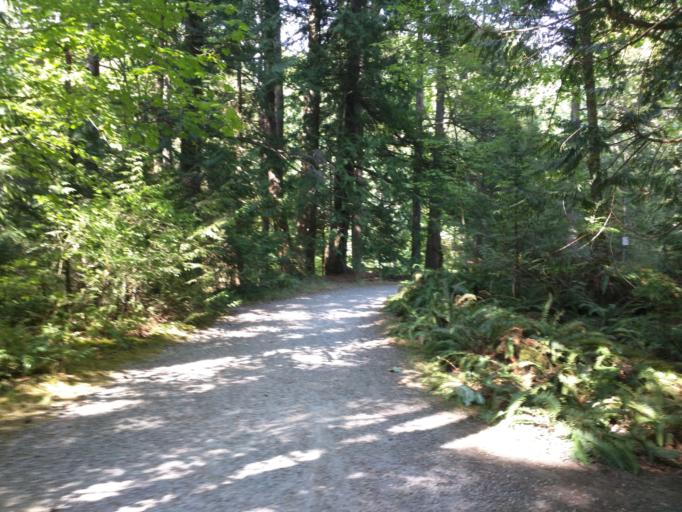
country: US
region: Washington
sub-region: Whatcom County
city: Geneva
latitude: 48.7534
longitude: -122.4277
